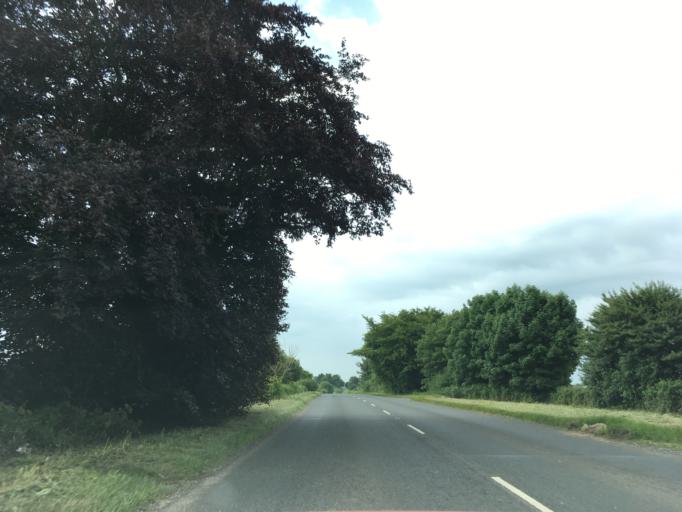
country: GB
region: England
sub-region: Gloucestershire
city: Nailsworth
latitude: 51.6601
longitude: -2.2326
